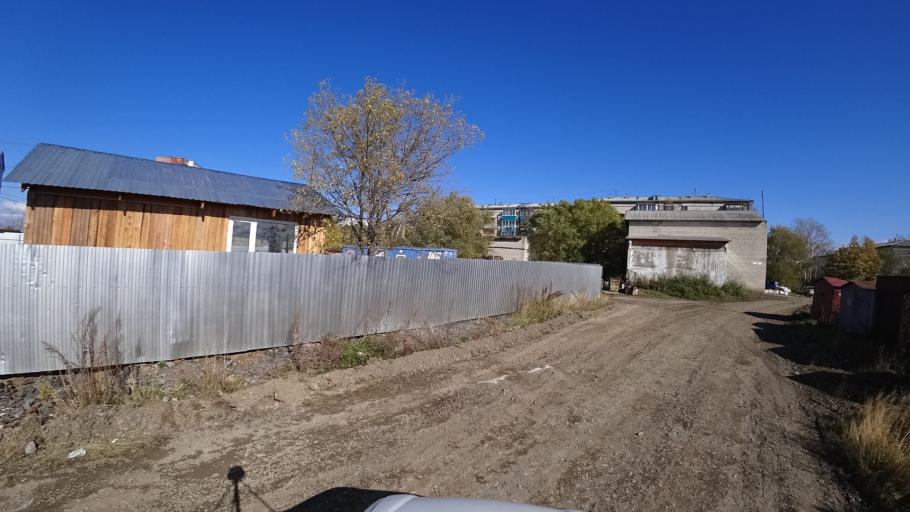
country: RU
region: Khabarovsk Krai
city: Amursk
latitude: 50.2164
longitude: 136.8910
